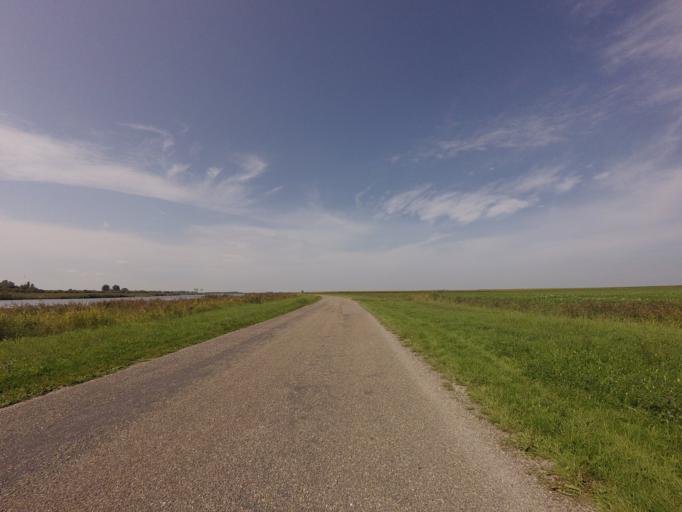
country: NL
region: Groningen
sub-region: Gemeente De Marne
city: Ulrum
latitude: 53.3414
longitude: 6.2898
